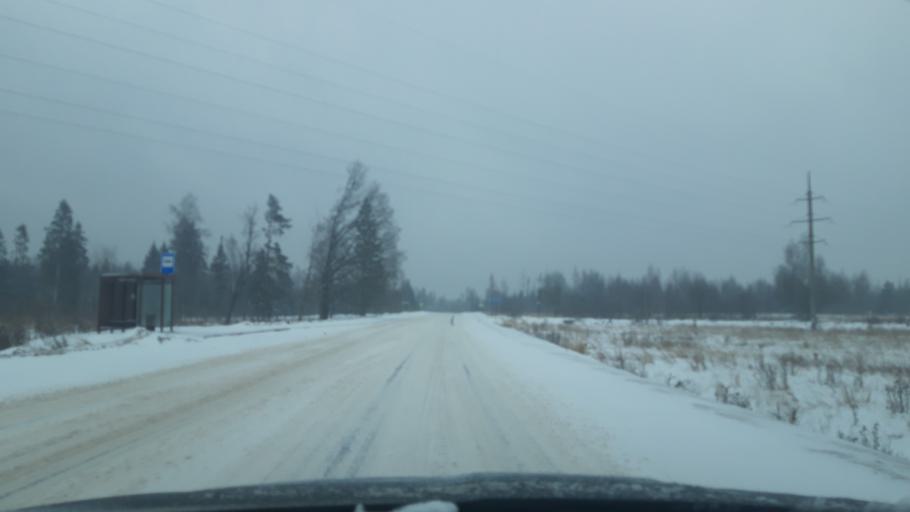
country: RU
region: Moskovskaya
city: Avtopoligon
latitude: 56.2655
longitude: 37.2635
